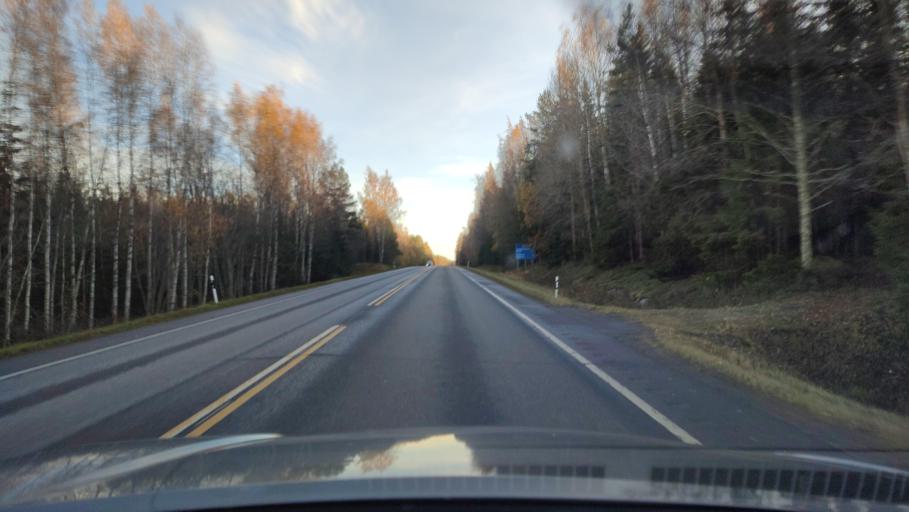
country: FI
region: Ostrobothnia
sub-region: Vaasa
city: Ristinummi
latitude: 63.0169
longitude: 21.7593
